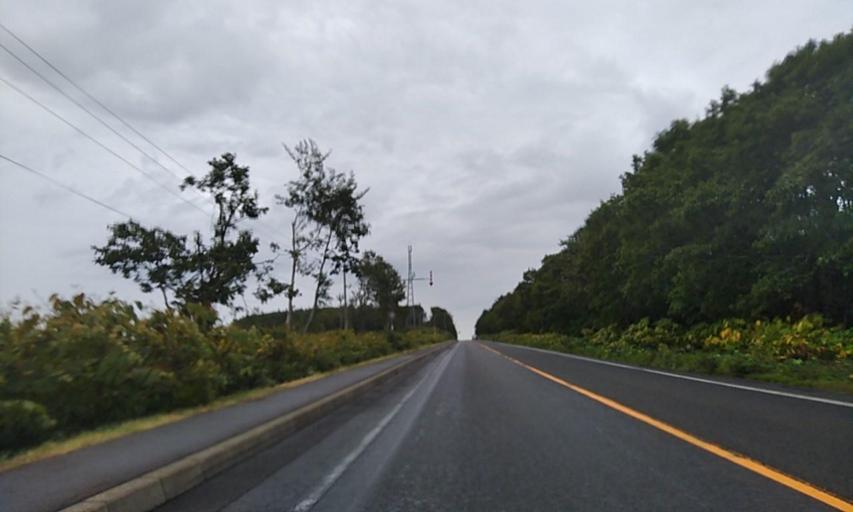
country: JP
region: Hokkaido
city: Mombetsu
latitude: 44.5244
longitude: 143.0500
